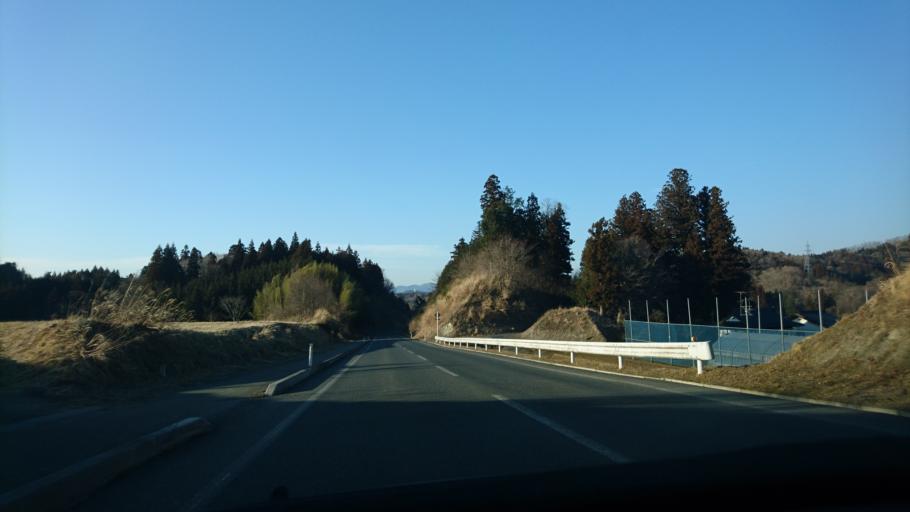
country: JP
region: Iwate
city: Ichinoseki
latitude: 38.9253
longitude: 141.3626
